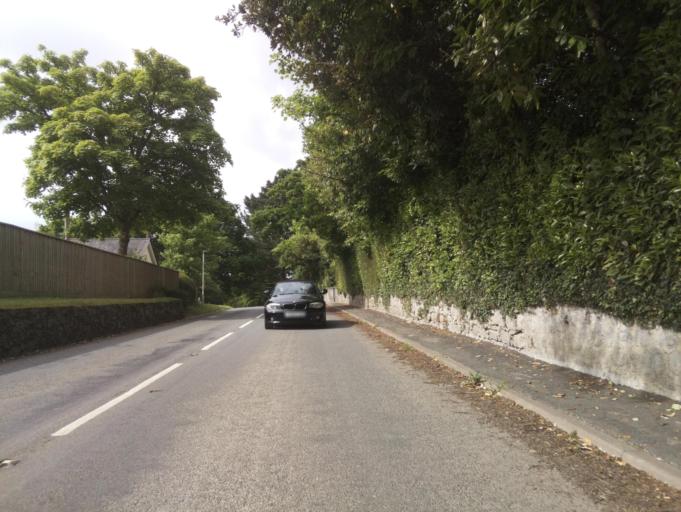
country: GB
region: England
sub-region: Devon
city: Chudleigh
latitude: 50.6118
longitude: -3.5910
